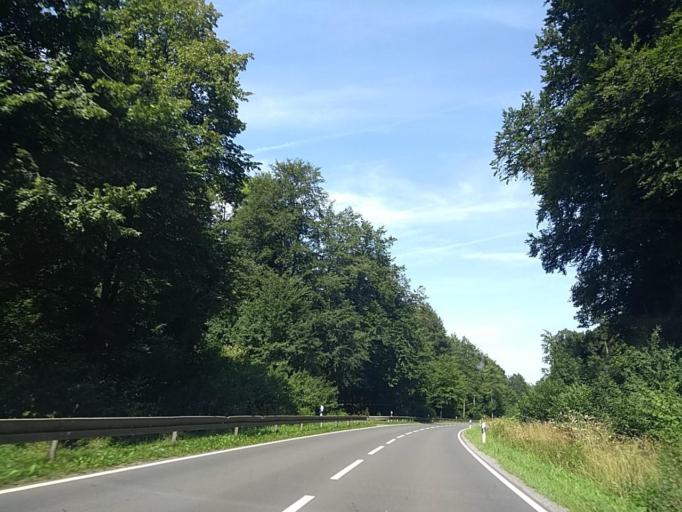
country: DE
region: North Rhine-Westphalia
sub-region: Regierungsbezirk Arnsberg
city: Brilon
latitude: 51.4504
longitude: 8.6311
